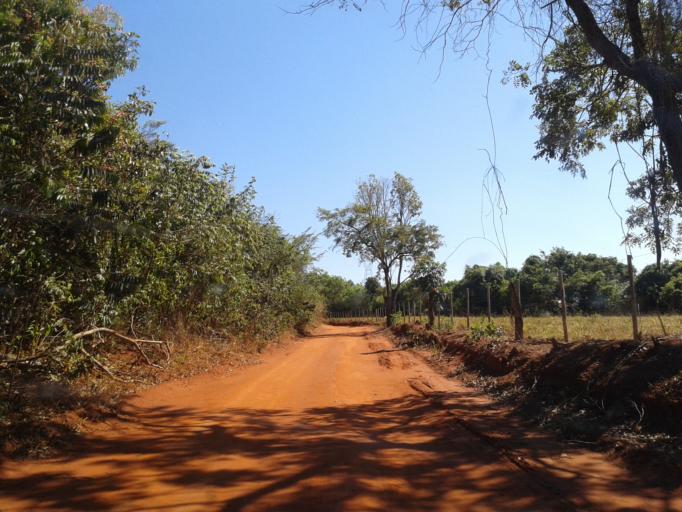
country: BR
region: Minas Gerais
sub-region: Monte Alegre De Minas
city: Monte Alegre de Minas
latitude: -18.8774
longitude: -49.1308
